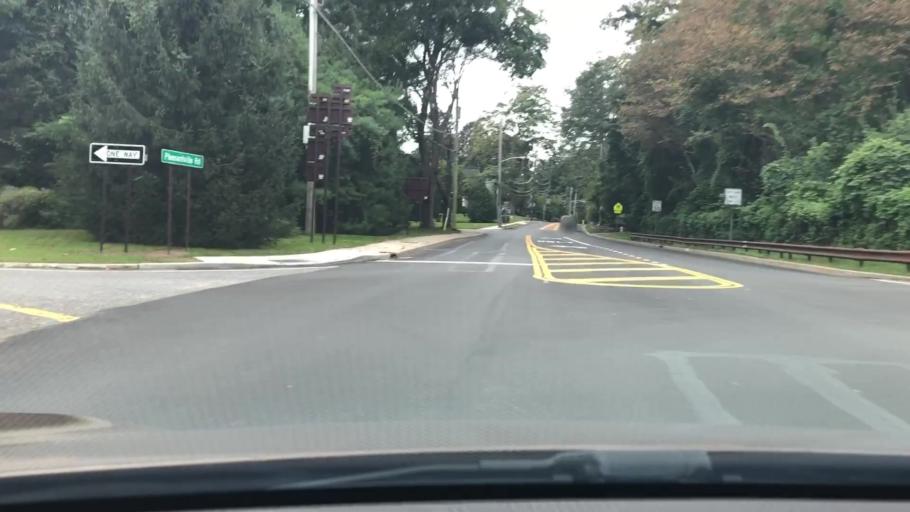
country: US
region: New York
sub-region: Westchester County
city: Briarcliff Manor
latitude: 41.1450
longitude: -73.8163
